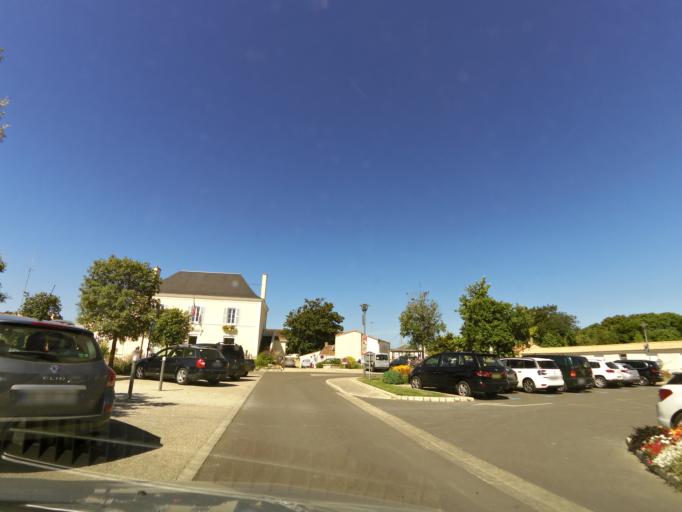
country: FR
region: Pays de la Loire
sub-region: Departement de la Vendee
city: Jard-sur-Mer
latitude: 46.4170
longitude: -1.5770
